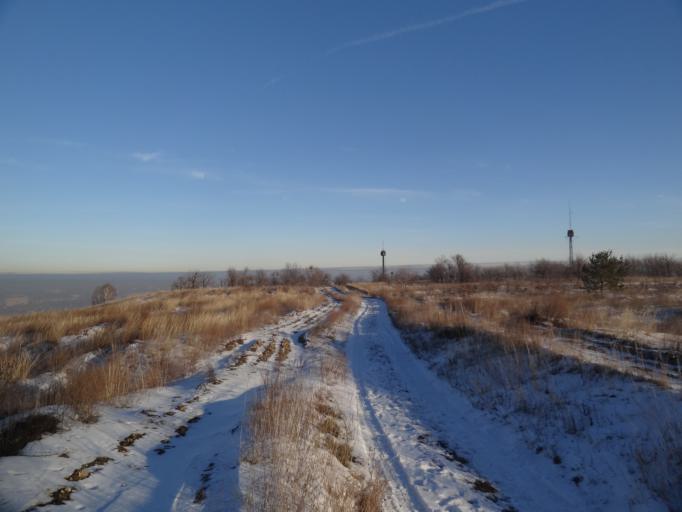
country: RU
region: Saratov
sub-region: Saratovskiy Rayon
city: Saratov
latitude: 51.5526
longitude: 45.9796
